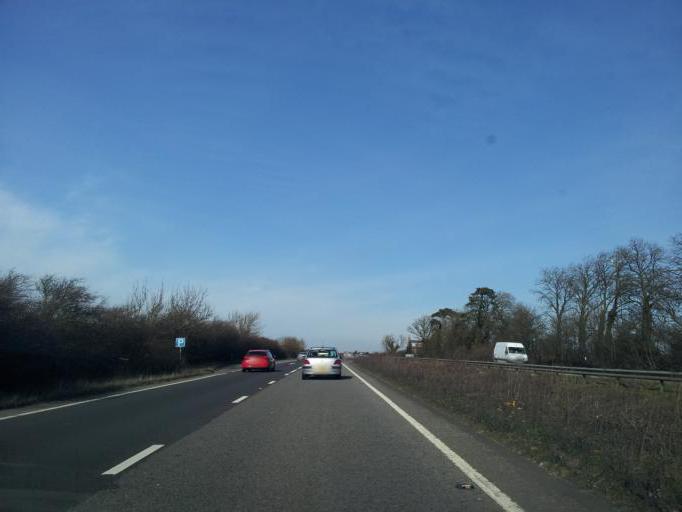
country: GB
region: England
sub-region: District of Rutland
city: Greetham
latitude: 52.7785
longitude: -0.6112
